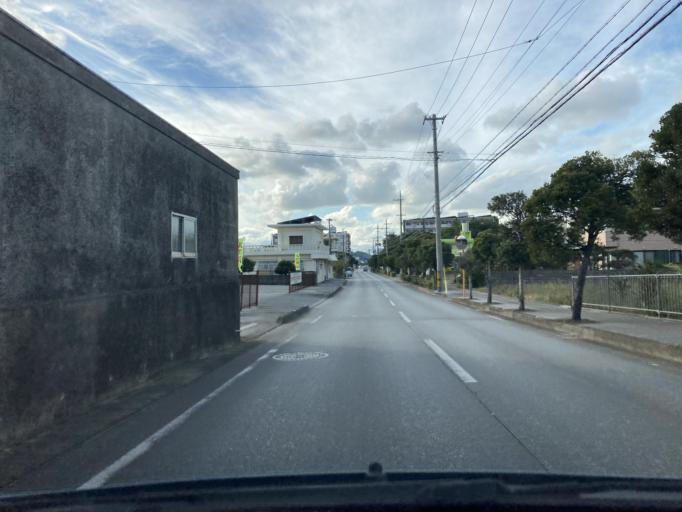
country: JP
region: Okinawa
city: Tomigusuku
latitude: 26.1458
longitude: 127.7315
